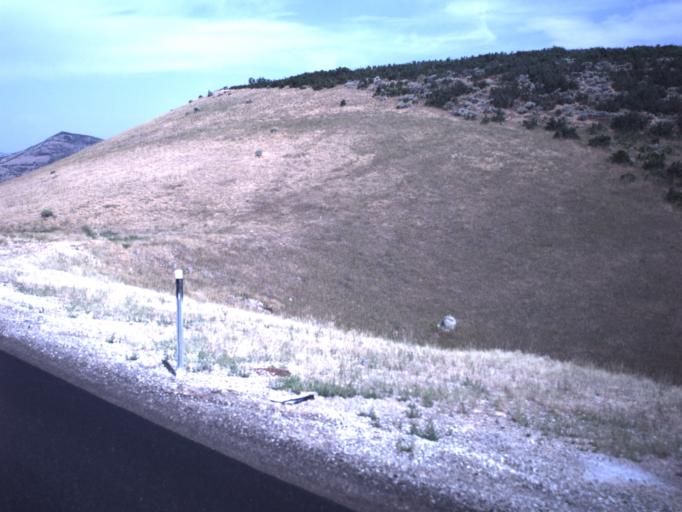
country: US
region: Utah
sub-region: Summit County
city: Park City
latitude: 40.6340
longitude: -111.3905
